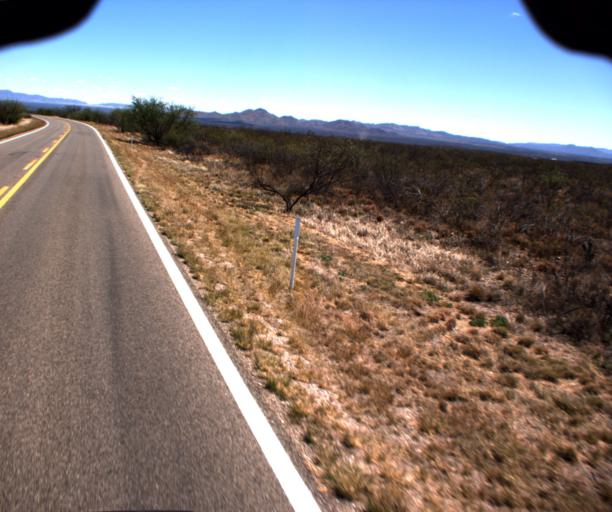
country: US
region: Arizona
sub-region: Cochise County
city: Huachuca City
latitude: 31.7135
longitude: -110.2550
